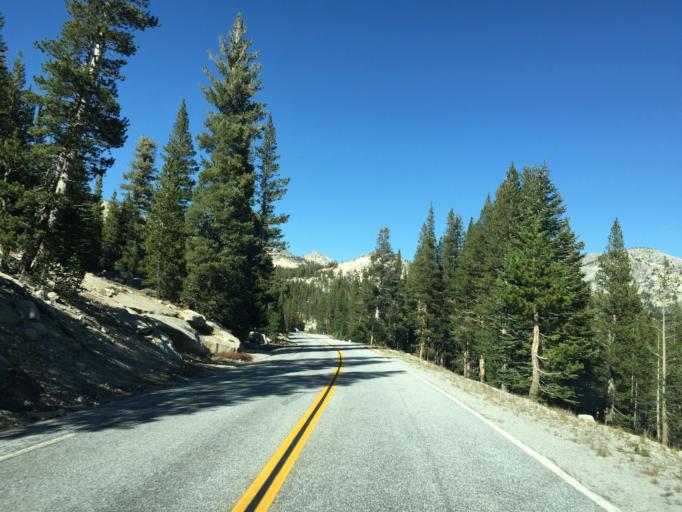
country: US
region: California
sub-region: Mariposa County
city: Yosemite Valley
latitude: 37.8197
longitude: -119.4782
